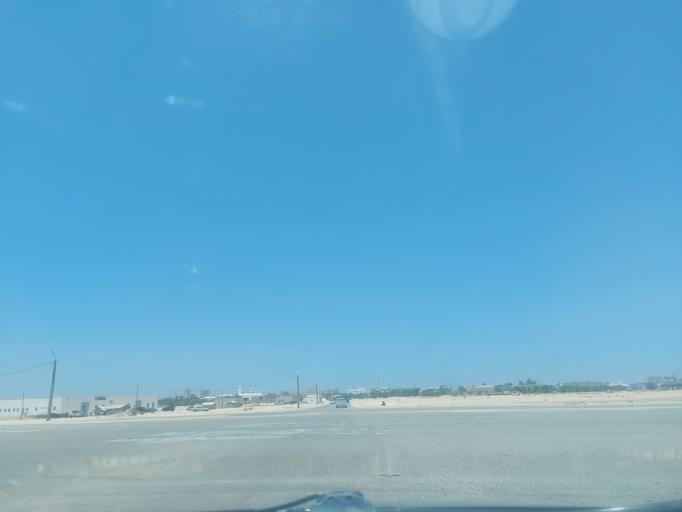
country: MR
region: Nouakchott
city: Nouakchott
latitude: 18.0874
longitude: -15.9563
